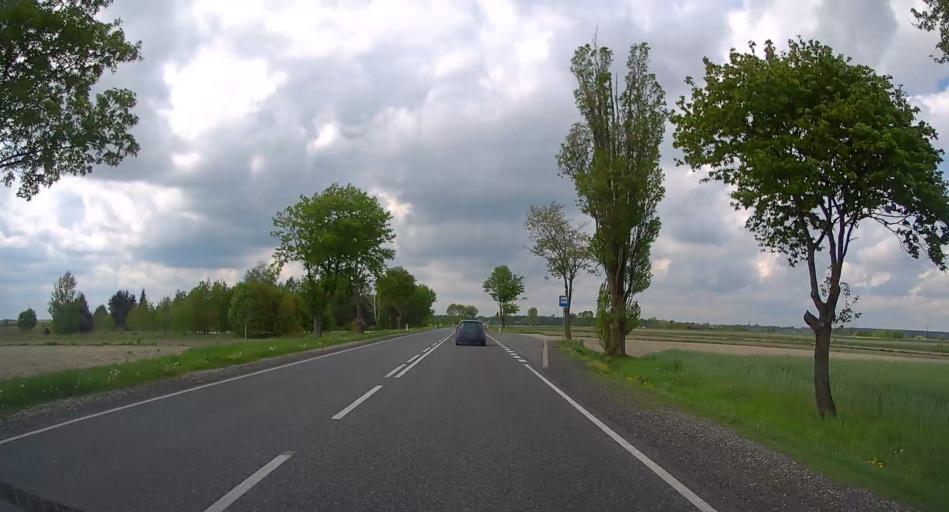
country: PL
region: Masovian Voivodeship
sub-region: Powiat nowodworski
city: Zakroczym
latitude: 52.4409
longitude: 20.5646
